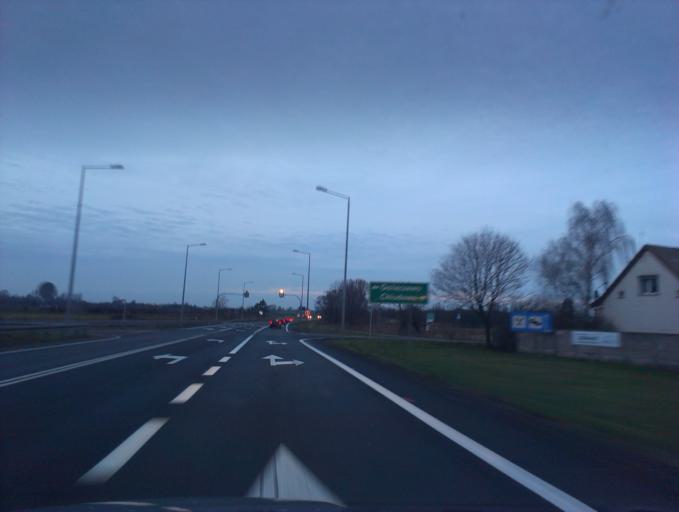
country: PL
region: Greater Poland Voivodeship
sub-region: Powiat poznanski
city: Zlotniki
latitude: 52.5519
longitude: 16.8369
